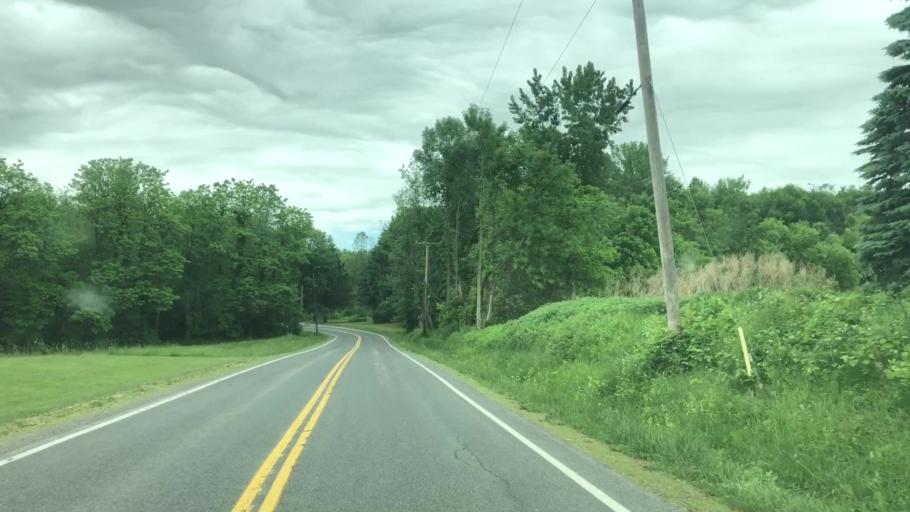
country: US
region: New York
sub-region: Wayne County
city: Macedon
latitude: 43.1170
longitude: -77.2878
